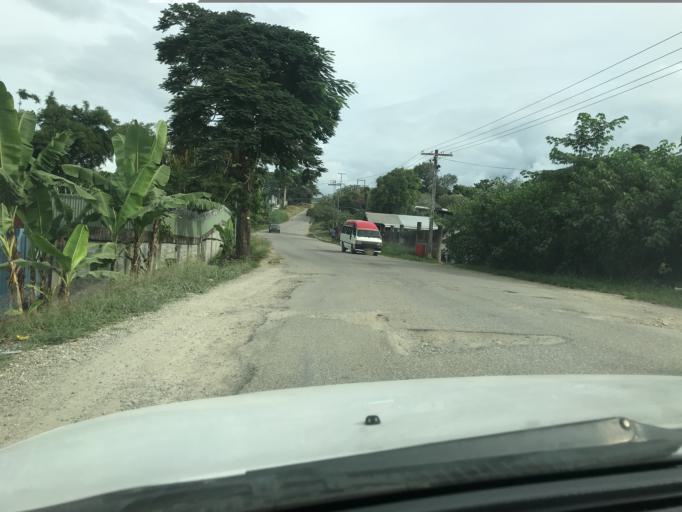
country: SB
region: Guadalcanal
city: Honiara
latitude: -9.4345
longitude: 159.9451
